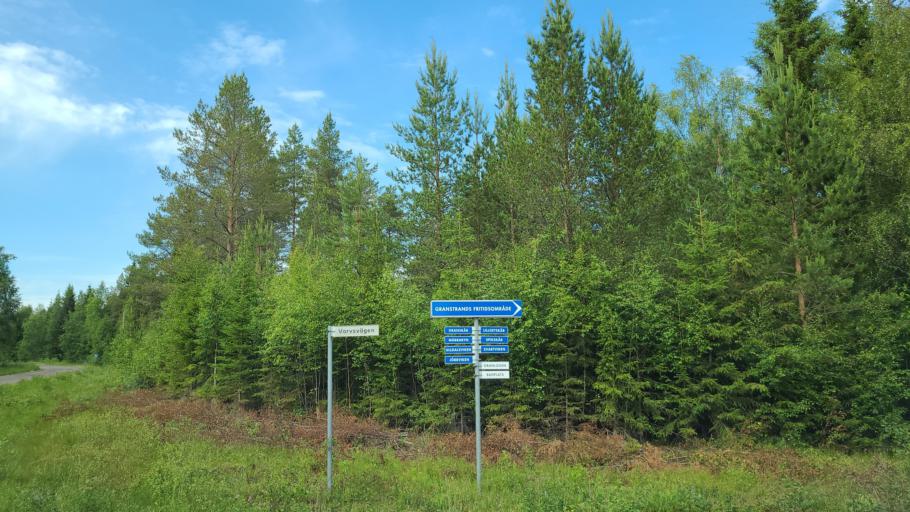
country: SE
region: Vaesterbotten
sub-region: Robertsfors Kommun
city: Robertsfors
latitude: 64.1642
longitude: 20.9710
